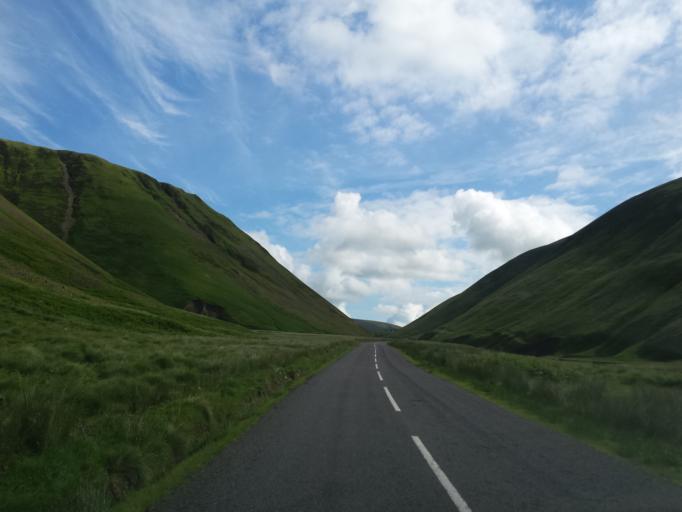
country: GB
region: Scotland
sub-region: Dumfries and Galloway
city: Moffat
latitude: 55.4148
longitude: -3.2922
